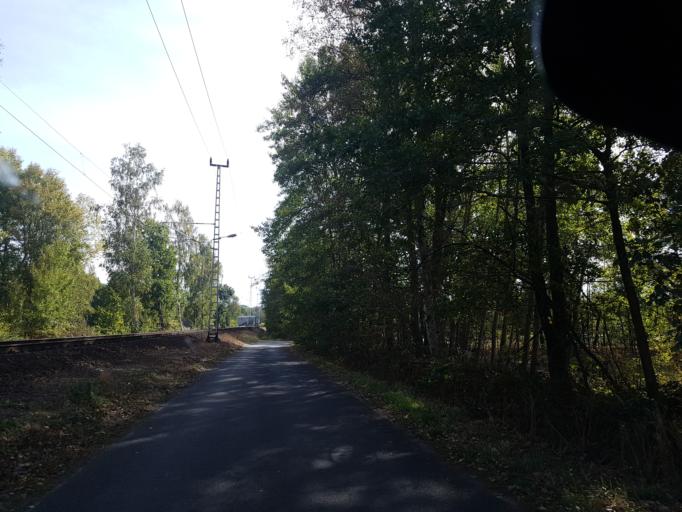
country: DE
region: Brandenburg
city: Doberlug-Kirchhain
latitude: 51.6330
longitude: 13.5859
